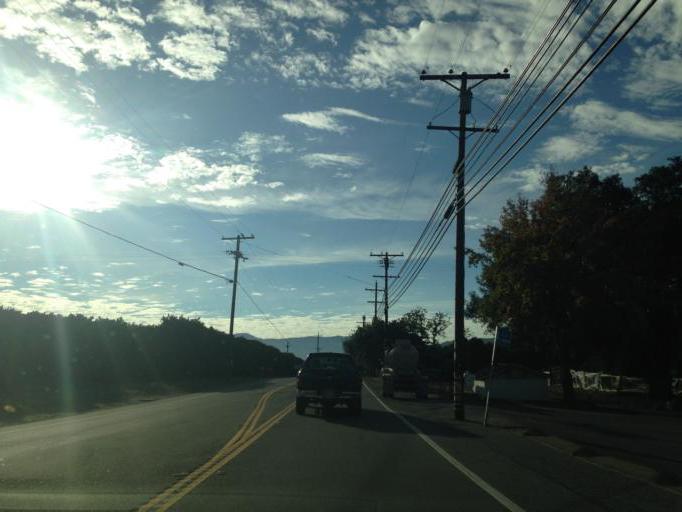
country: US
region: California
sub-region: San Diego County
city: Valley Center
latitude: 33.3296
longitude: -117.0007
